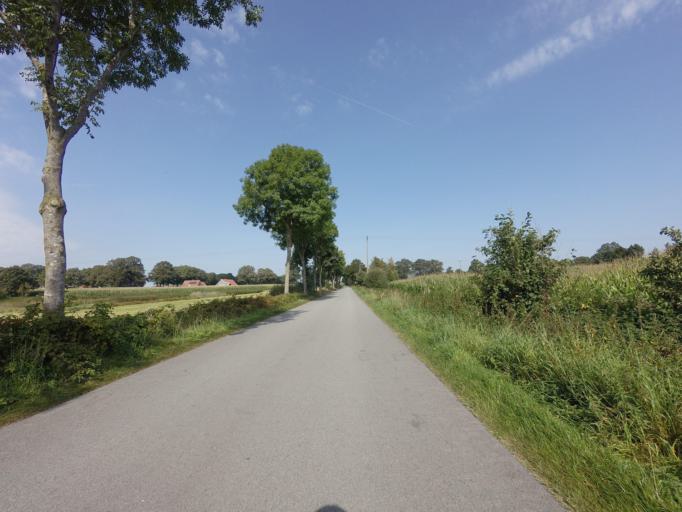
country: DE
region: Lower Saxony
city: Itterbeck
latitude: 52.5342
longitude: 6.7677
